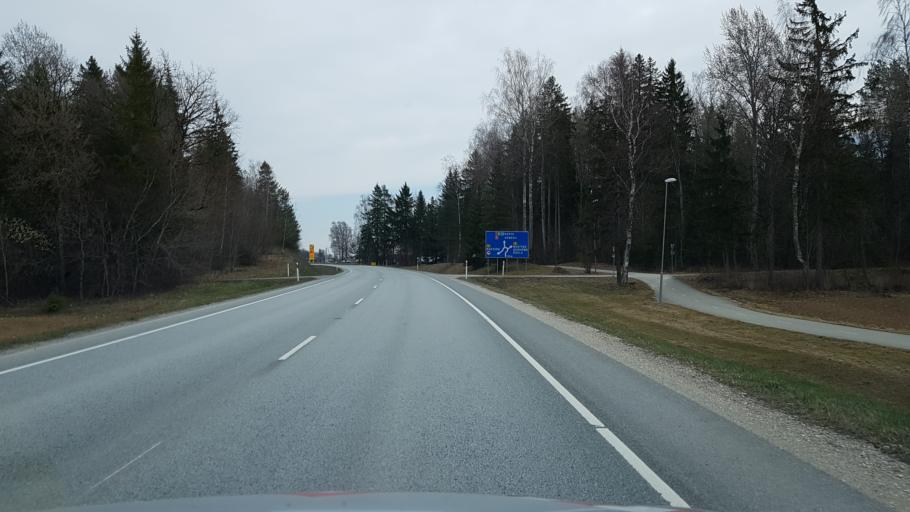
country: EE
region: Laeaene-Virumaa
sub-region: Rakvere linn
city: Rakvere
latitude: 59.3208
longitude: 26.3640
